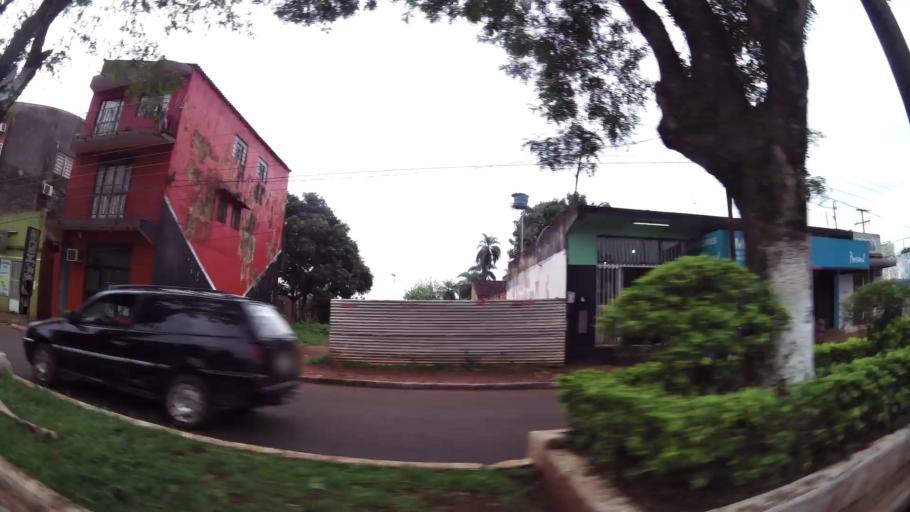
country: PY
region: Alto Parana
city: Ciudad del Este
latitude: -25.4072
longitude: -54.6362
